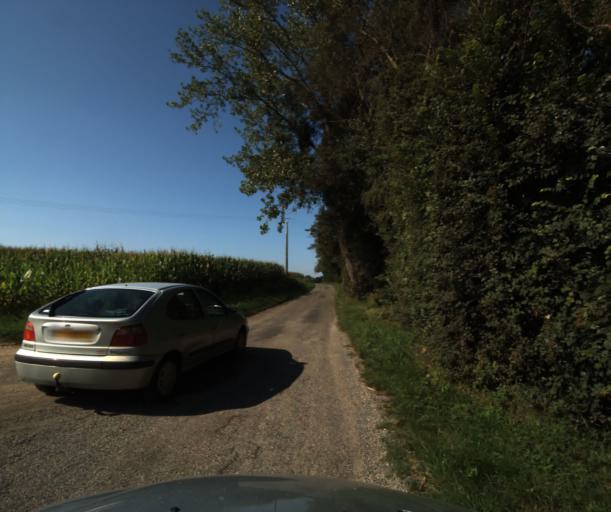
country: FR
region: Midi-Pyrenees
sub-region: Departement de la Haute-Garonne
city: Le Fauga
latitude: 43.4151
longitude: 1.3054
